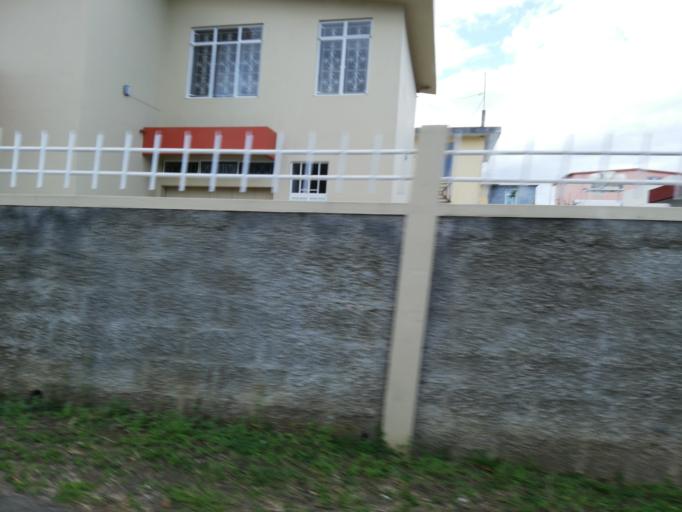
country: MU
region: Plaines Wilhems
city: Ebene
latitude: -20.2347
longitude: 57.4578
